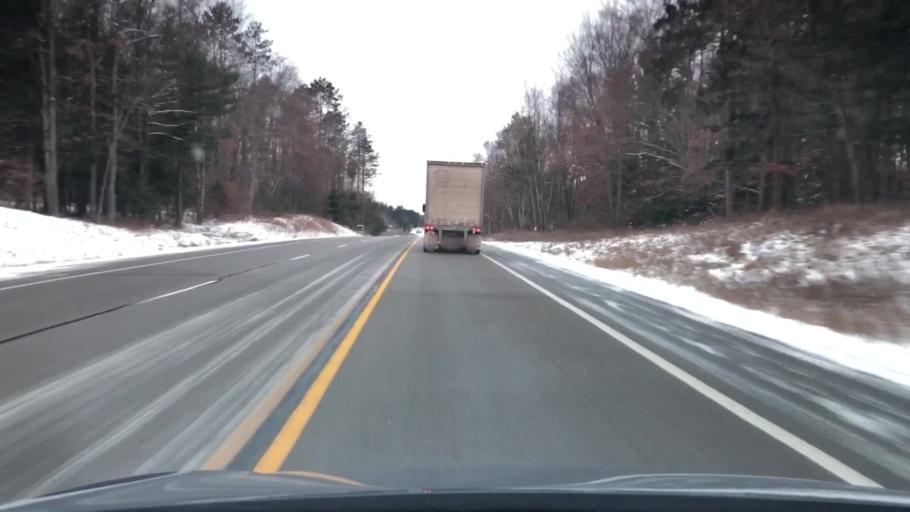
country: US
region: Michigan
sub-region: Wexford County
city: Cadillac
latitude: 44.1877
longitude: -85.3895
